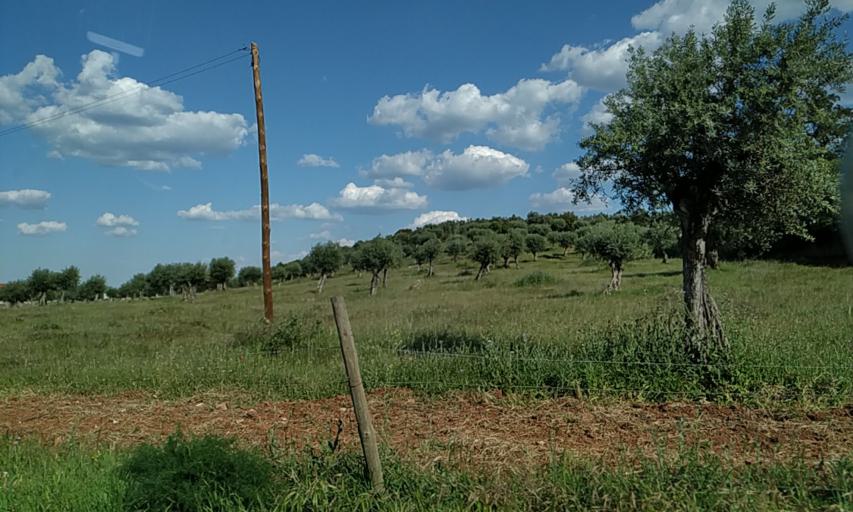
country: PT
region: Evora
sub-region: Estremoz
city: Estremoz
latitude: 38.8558
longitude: -7.5798
